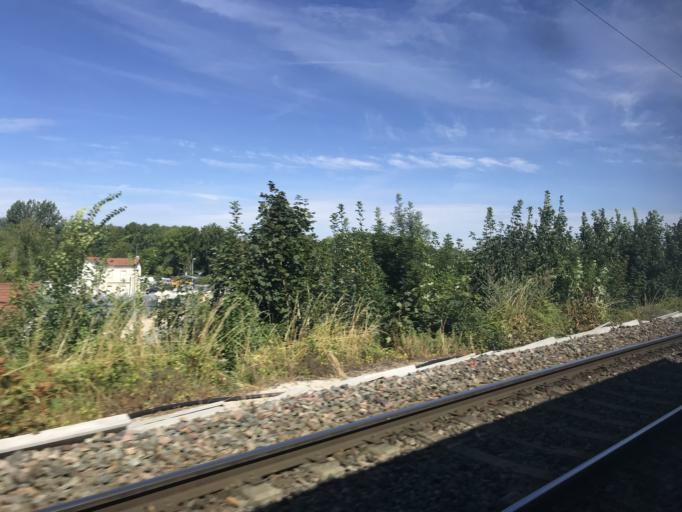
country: FR
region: Champagne-Ardenne
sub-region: Departement de la Marne
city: Reims
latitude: 49.2504
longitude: 4.0138
